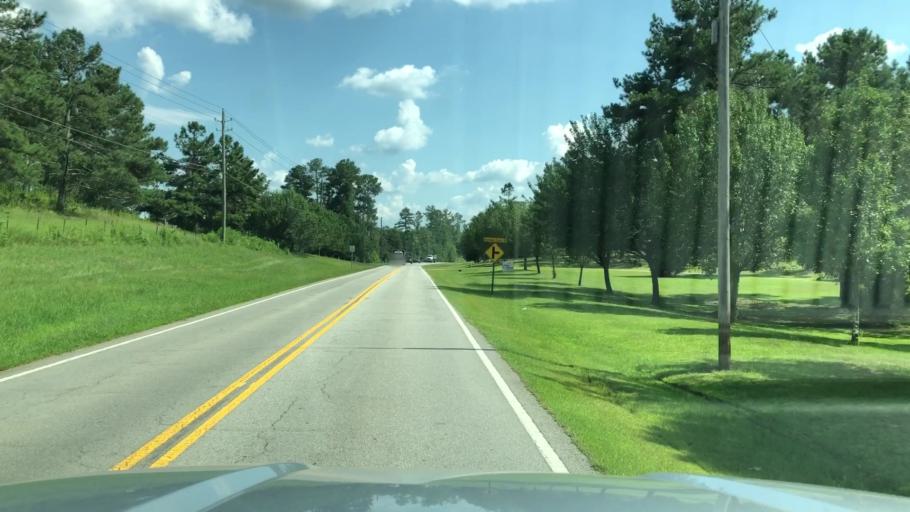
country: US
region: Georgia
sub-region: Paulding County
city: Dallas
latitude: 33.9497
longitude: -84.8420
